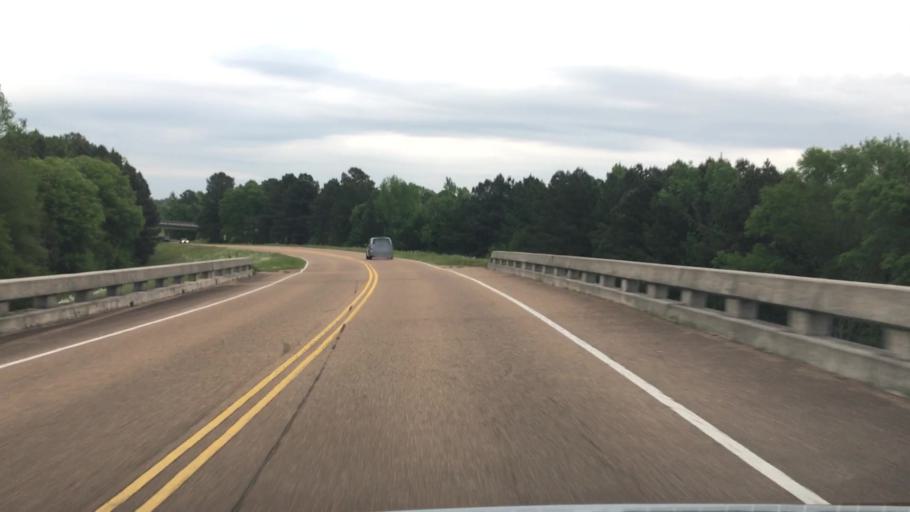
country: US
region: Mississippi
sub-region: Hinds County
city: Clinton
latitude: 32.3818
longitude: -90.2595
